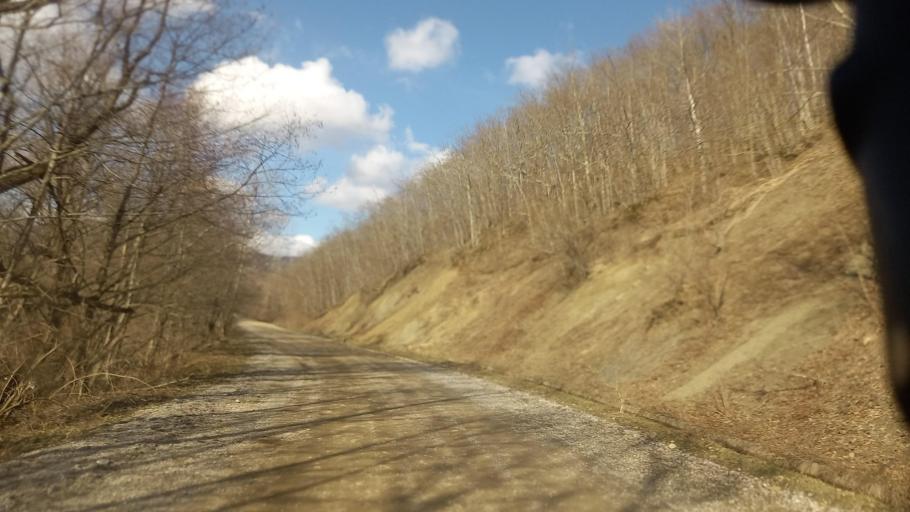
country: RU
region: Krasnodarskiy
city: Smolenskaya
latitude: 44.6081
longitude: 38.8374
